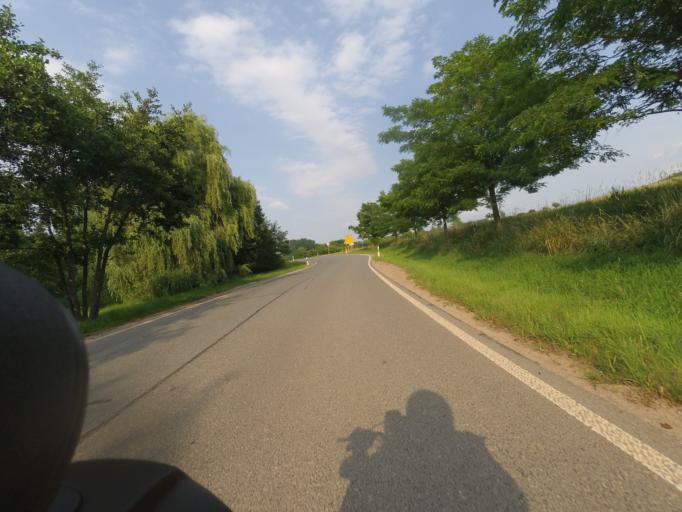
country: DE
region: Saxony
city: Wilsdruff
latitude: 51.0496
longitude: 13.5492
